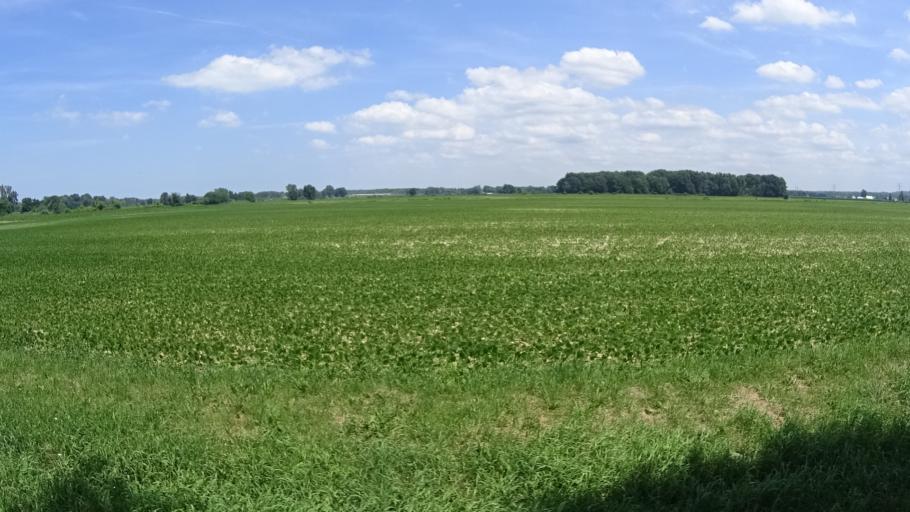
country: US
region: Ohio
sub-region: Erie County
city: Huron
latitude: 41.3613
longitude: -82.5382
